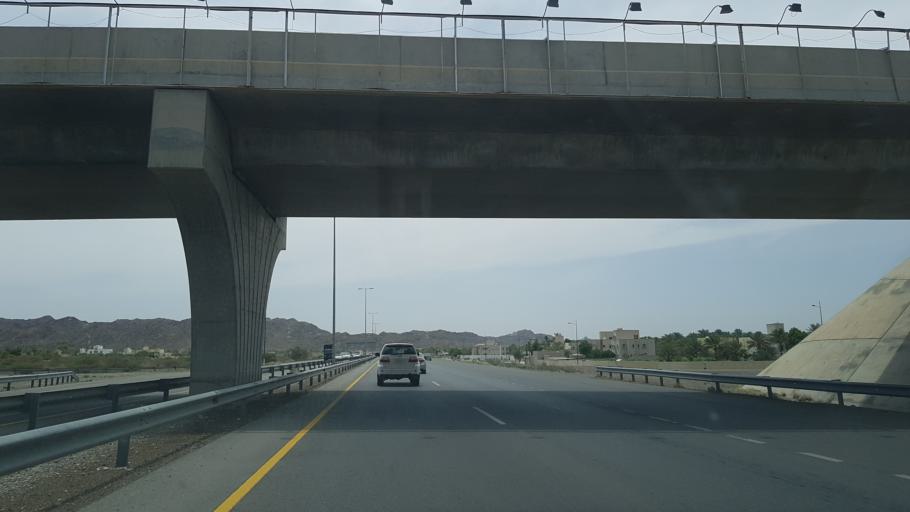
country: OM
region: Muhafazat ad Dakhiliyah
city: Izki
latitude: 22.9980
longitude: 57.7913
